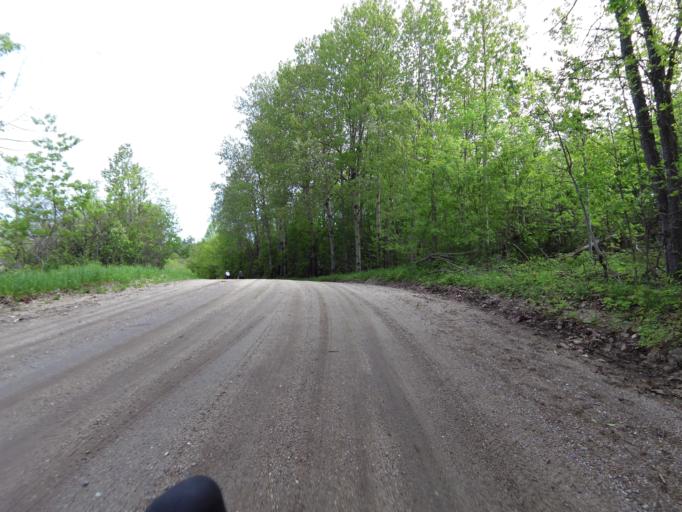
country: CA
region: Quebec
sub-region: Outaouais
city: Wakefield
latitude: 45.7652
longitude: -75.9173
